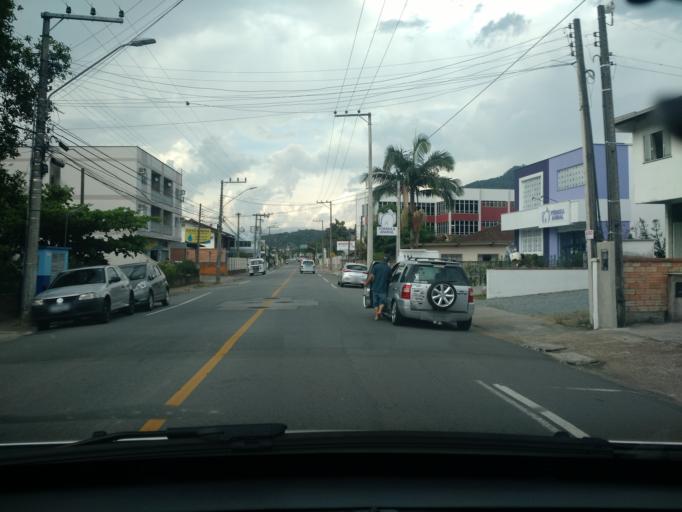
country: BR
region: Santa Catarina
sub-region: Jaragua Do Sul
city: Jaragua do Sul
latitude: -26.4868
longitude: -49.0923
